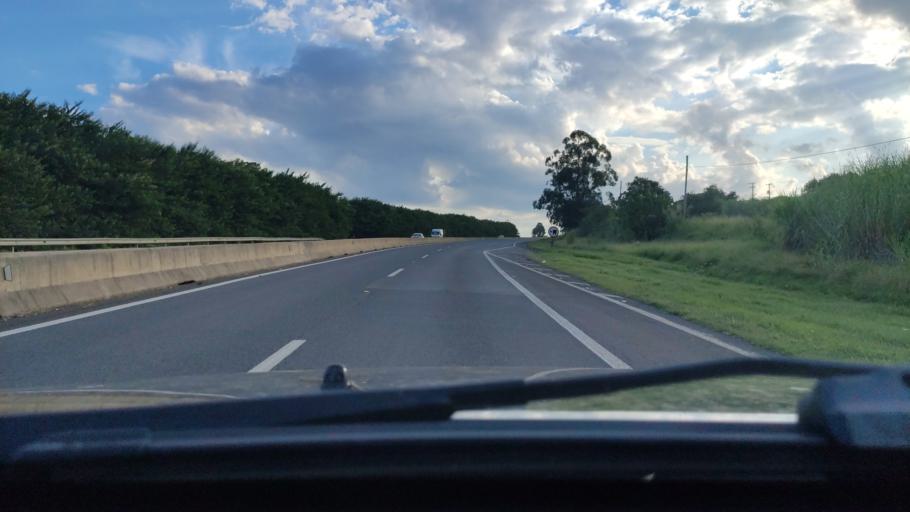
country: BR
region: Sao Paulo
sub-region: Mogi-Mirim
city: Mogi Mirim
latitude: -22.4484
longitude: -47.0583
